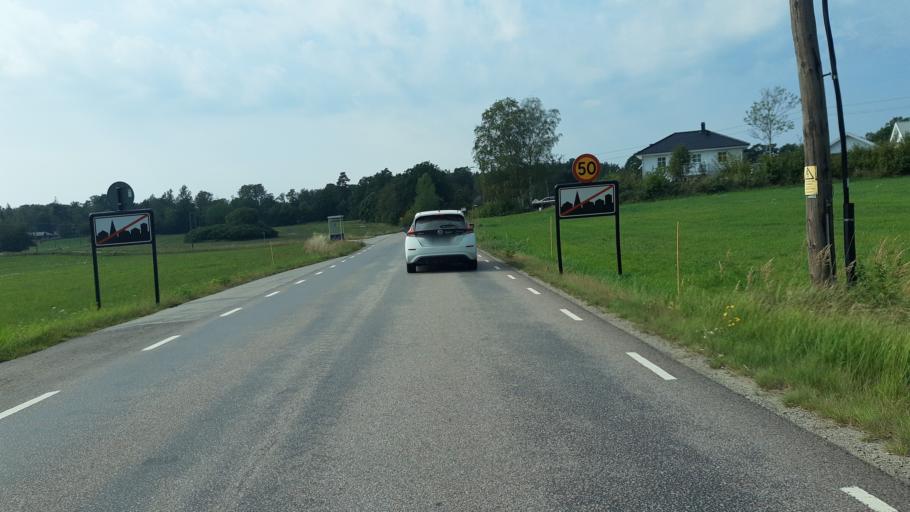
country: SE
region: Blekinge
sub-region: Karlskrona Kommun
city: Nattraby
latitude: 56.1880
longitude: 15.5290
